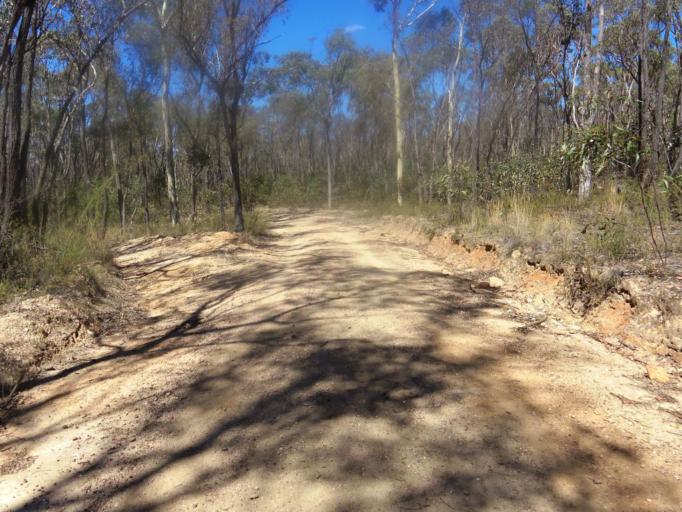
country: AU
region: Victoria
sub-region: Mount Alexander
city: Castlemaine
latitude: -37.0096
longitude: 144.1250
